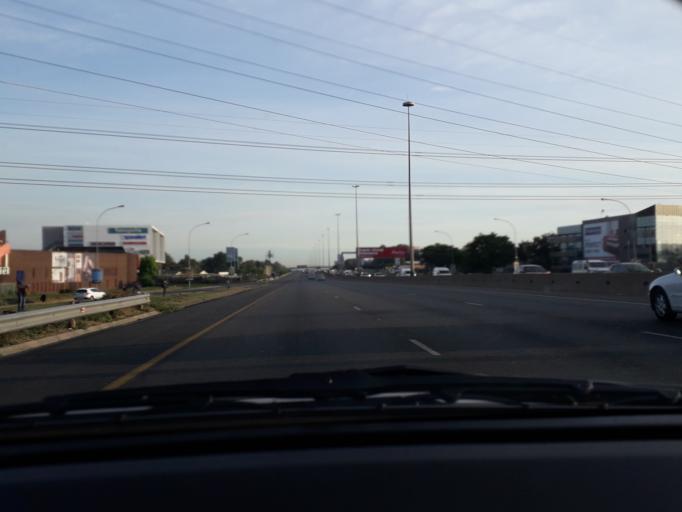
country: ZA
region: Gauteng
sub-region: City of Johannesburg Metropolitan Municipality
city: Modderfontein
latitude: -26.0901
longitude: 28.0856
